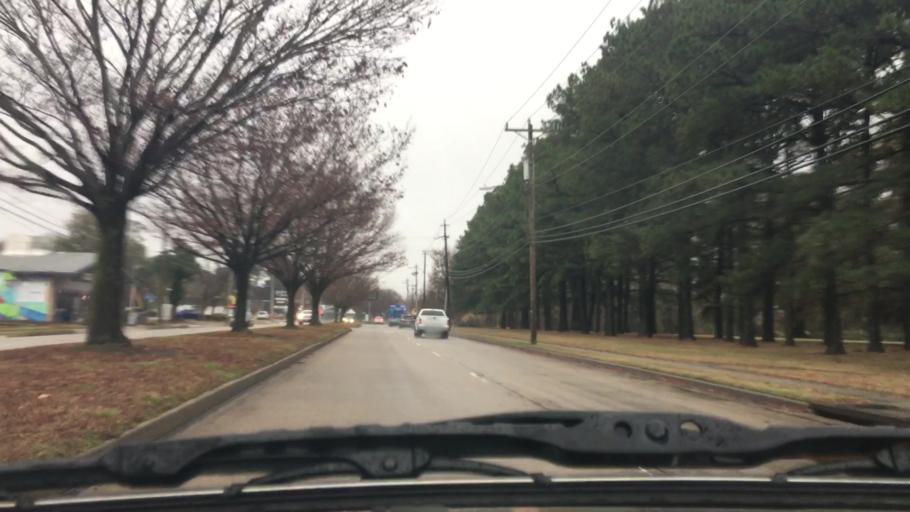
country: US
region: Virginia
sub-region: City of Norfolk
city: Norfolk
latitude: 36.9268
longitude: -76.2528
